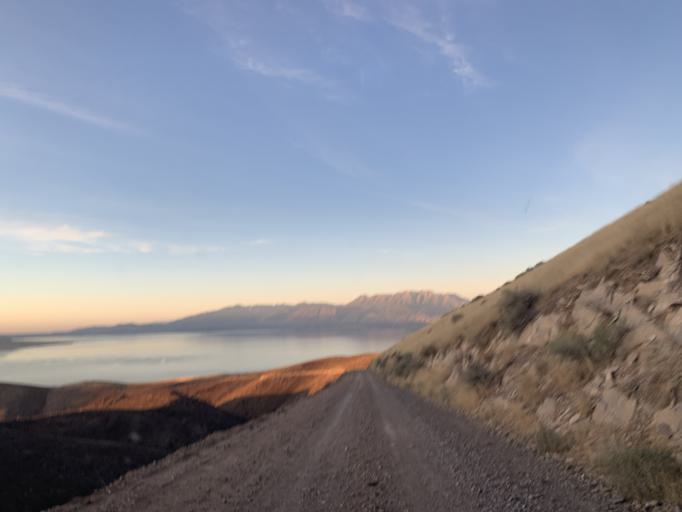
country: US
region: Utah
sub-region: Utah County
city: West Mountain
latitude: 40.1016
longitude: -111.8234
